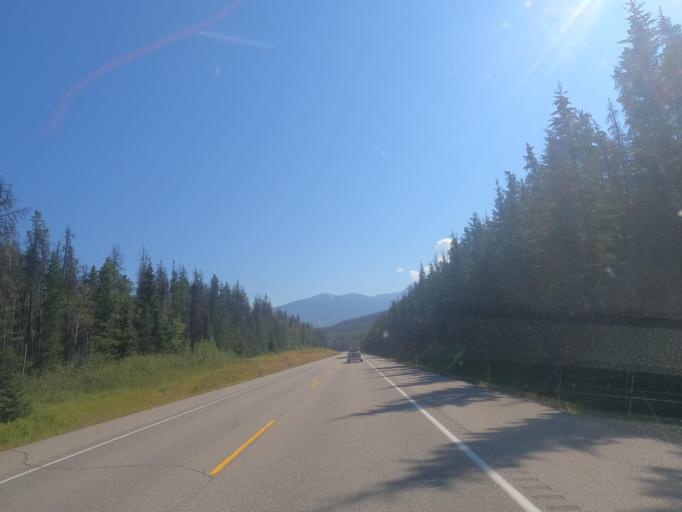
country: CA
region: Alberta
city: Jasper Park Lodge
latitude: 52.8574
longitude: -118.1279
